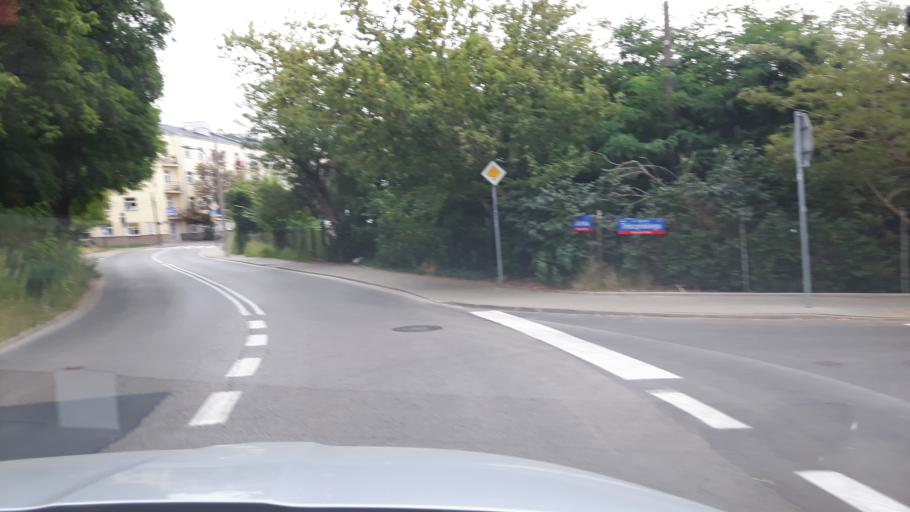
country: PL
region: Masovian Voivodeship
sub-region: Warszawa
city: Zoliborz
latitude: 52.2743
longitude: 20.9736
